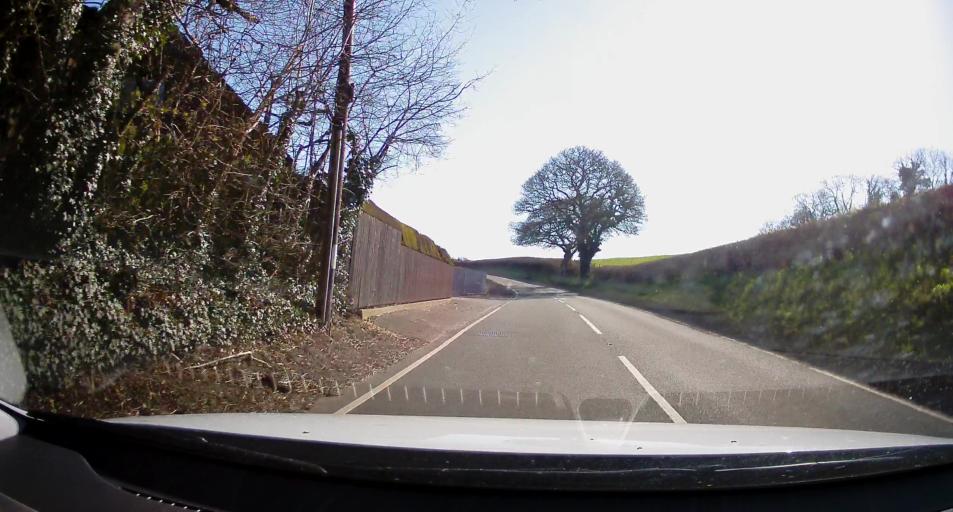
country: GB
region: Wales
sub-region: County of Ceredigion
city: Penparcau
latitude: 52.3754
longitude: -4.0726
